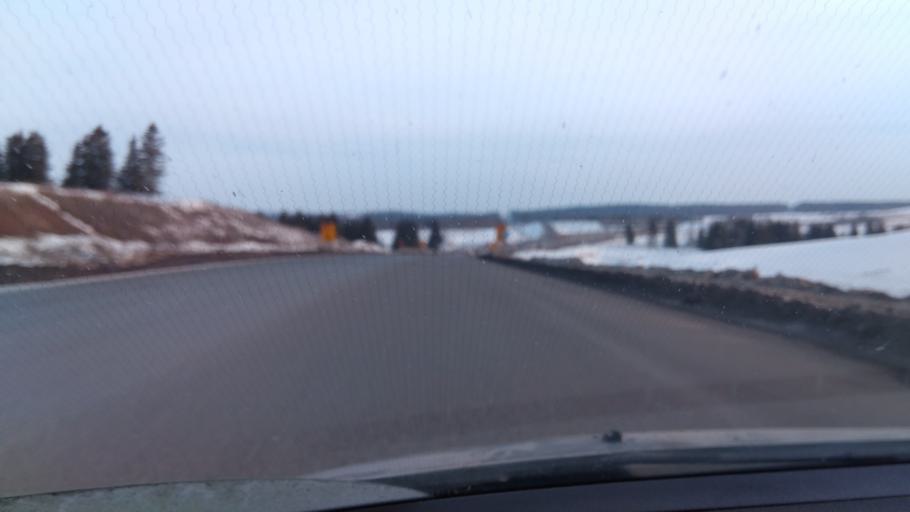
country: RU
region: Perm
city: Zvezdnyy
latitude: 57.7899
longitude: 56.3380
